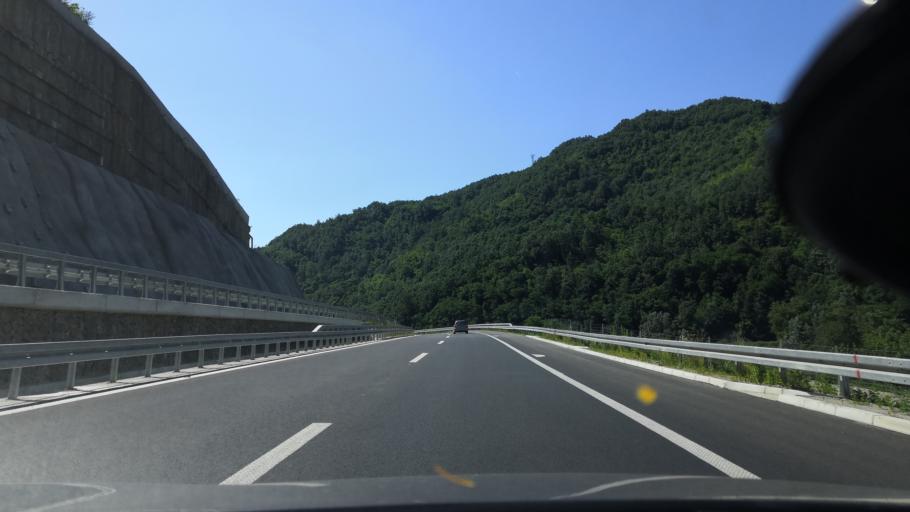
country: RS
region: Central Serbia
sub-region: Jablanicki Okrug
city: Vlasotince
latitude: 42.8705
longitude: 22.1022
